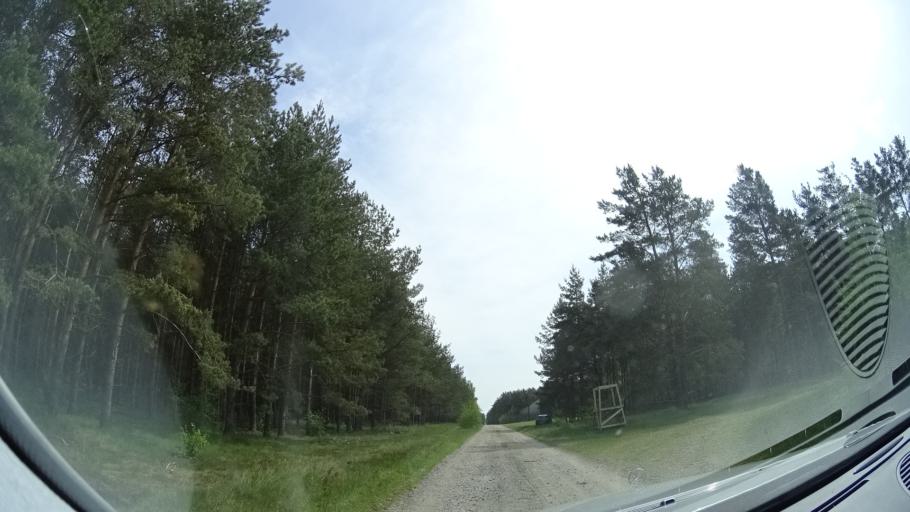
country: SE
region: Skane
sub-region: Sjobo Kommun
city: Sjoebo
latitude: 55.6717
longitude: 13.6335
